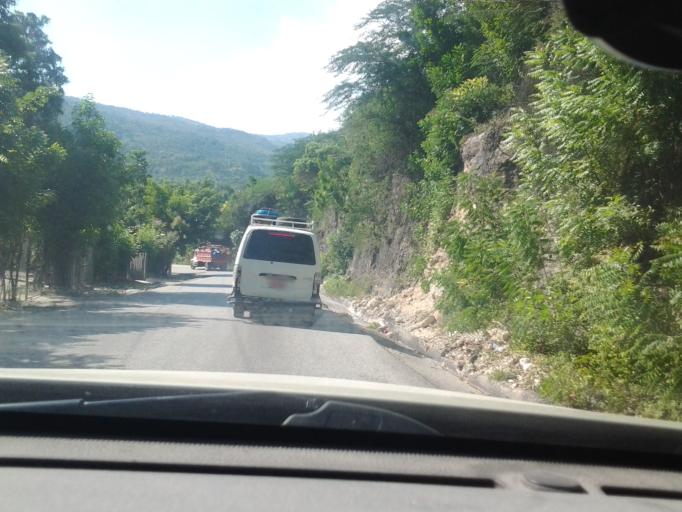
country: HT
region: Sud-Est
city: Jacmel
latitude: 18.2754
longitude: -72.5684
